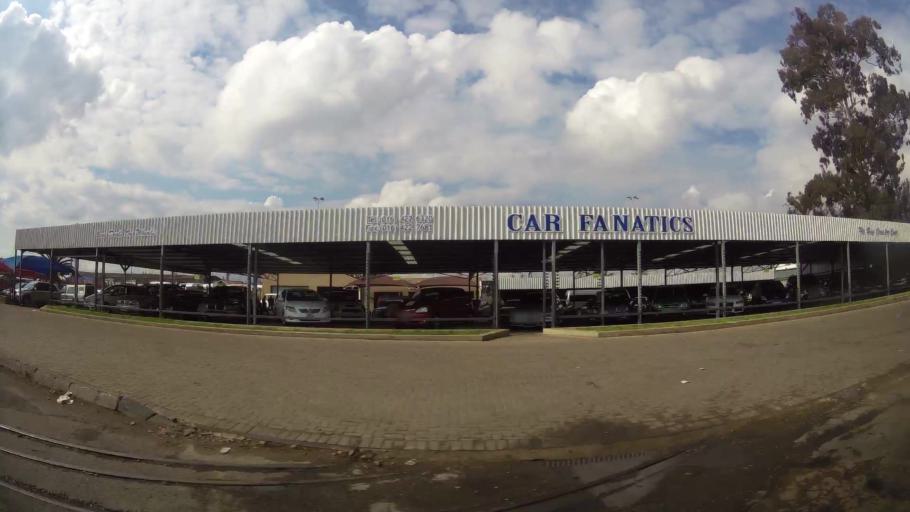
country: ZA
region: Gauteng
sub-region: Sedibeng District Municipality
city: Vereeniging
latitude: -26.6716
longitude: 27.9346
